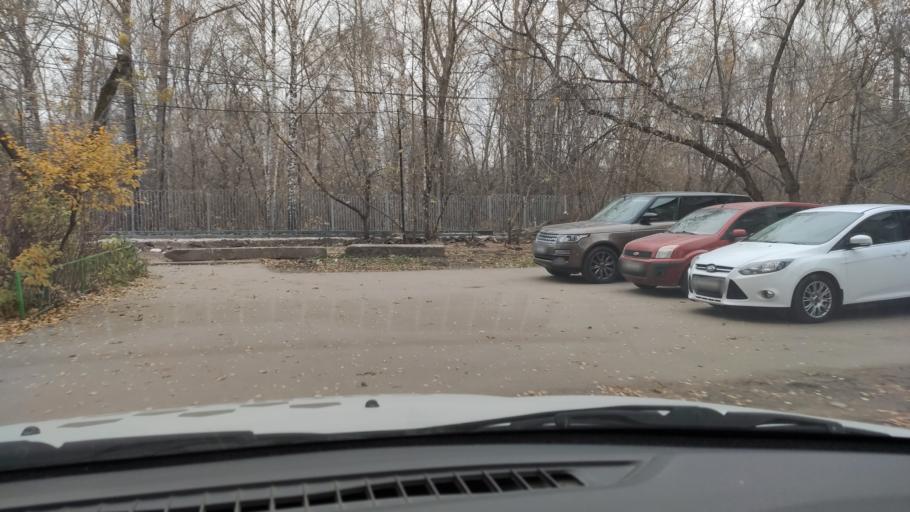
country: RU
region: Perm
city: Perm
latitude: 58.0086
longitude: 56.2723
